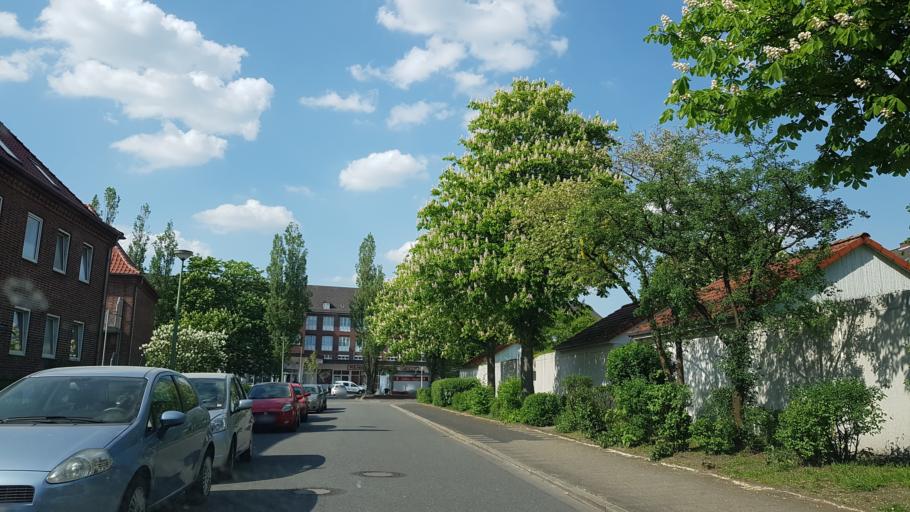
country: DE
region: Lower Saxony
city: Langen
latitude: 53.5789
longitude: 8.5954
